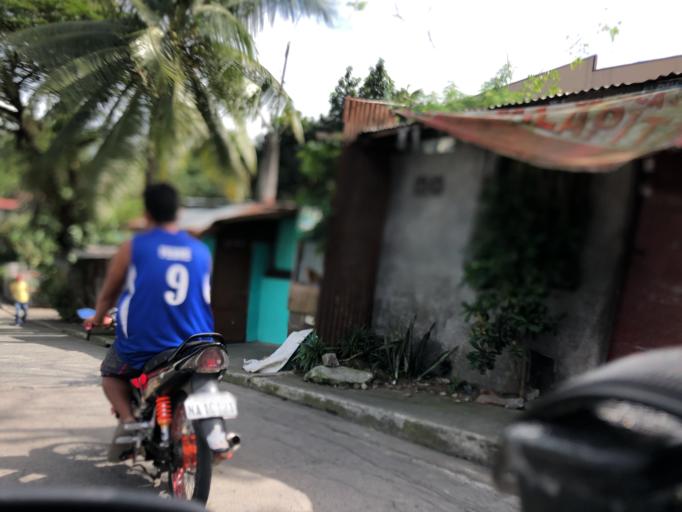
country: PH
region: Central Luzon
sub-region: Province of Bulacan
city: San Jose del Monte
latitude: 14.7580
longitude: 121.0532
